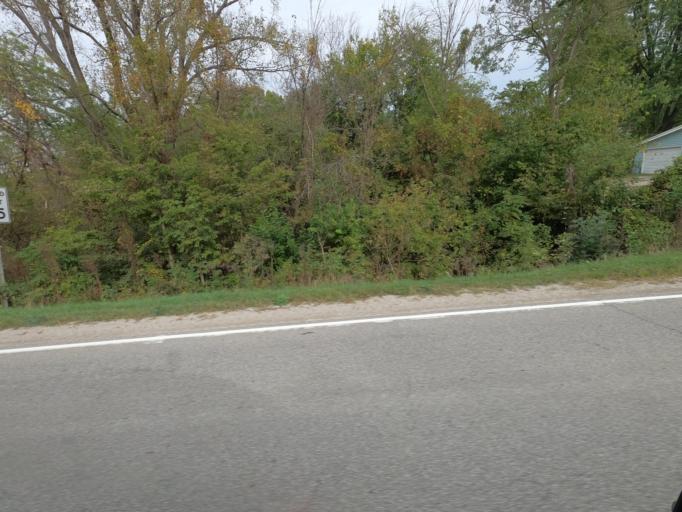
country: US
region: Iowa
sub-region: Jefferson County
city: Fairfield
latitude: 40.8733
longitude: -92.1535
